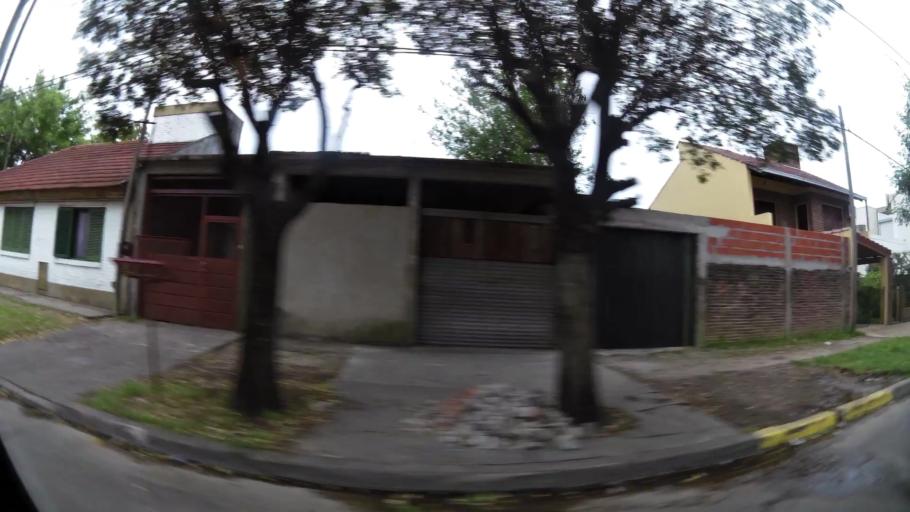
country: AR
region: Buenos Aires
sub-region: Partido de La Plata
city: La Plata
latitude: -34.9200
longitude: -57.9816
